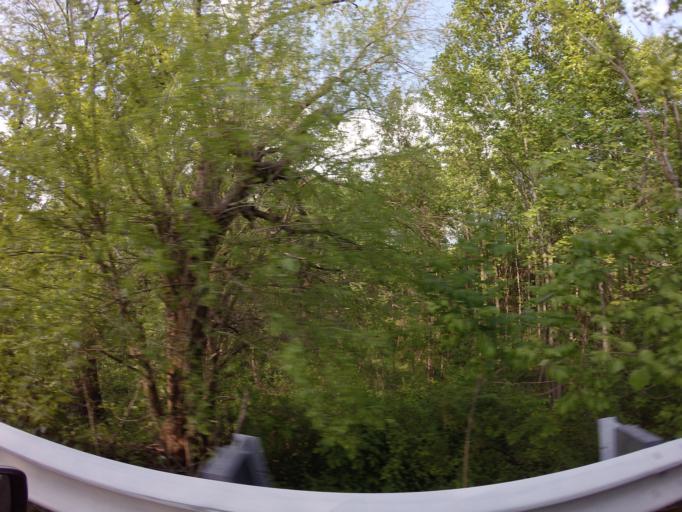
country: US
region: Maryland
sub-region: Baltimore County
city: Hunt Valley
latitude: 39.5130
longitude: -76.7050
